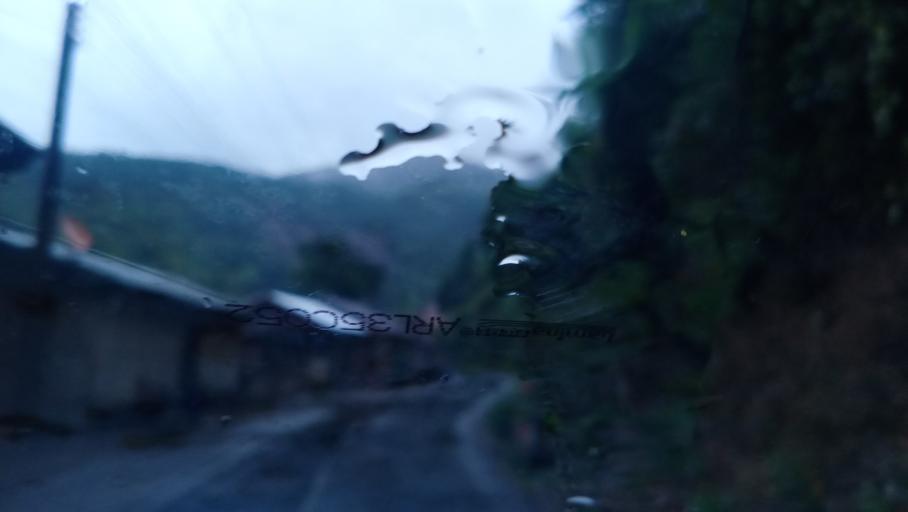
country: LA
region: Phongsali
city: Khoa
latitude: 21.0765
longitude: 102.5008
